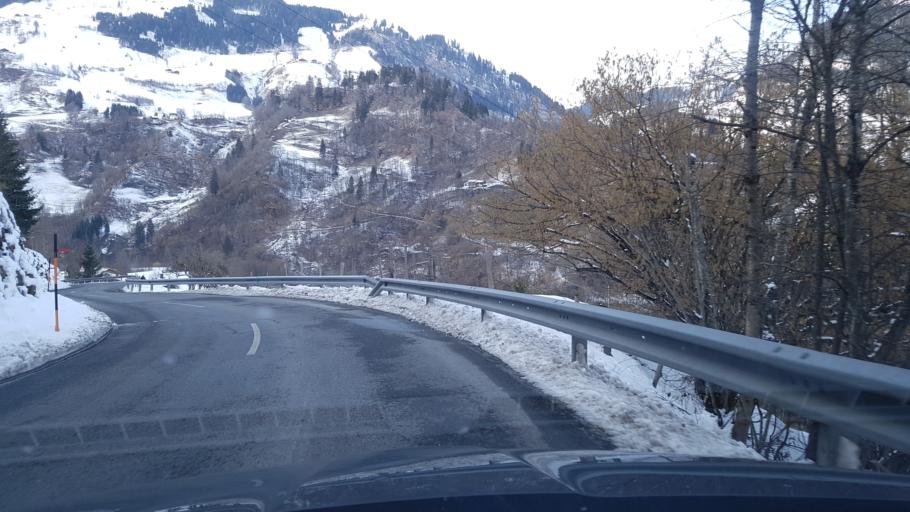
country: AT
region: Salzburg
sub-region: Politischer Bezirk Zell am See
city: Lend
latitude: 47.3026
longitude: 13.0304
